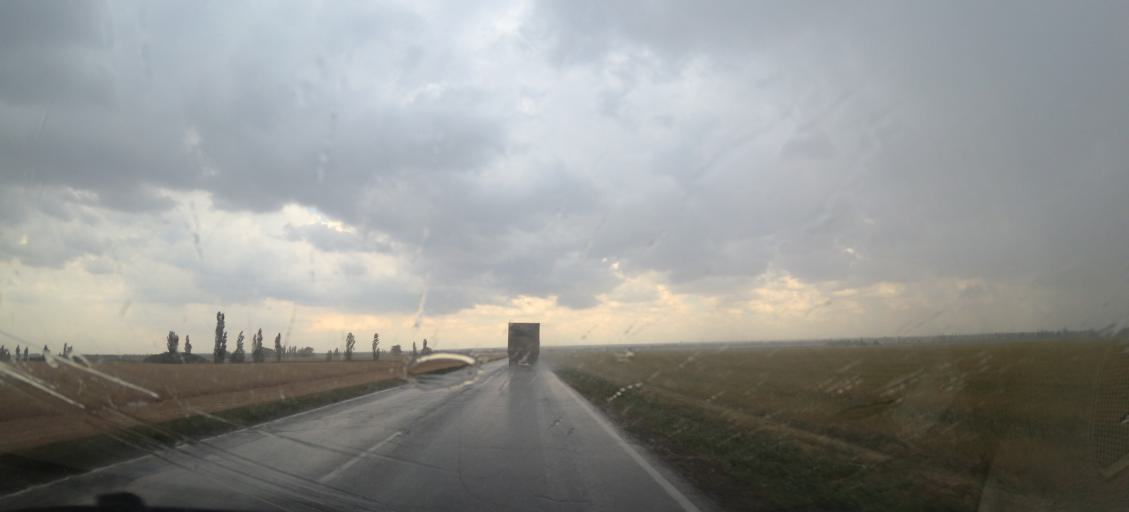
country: RU
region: Rostov
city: Orlovskiy
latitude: 46.8647
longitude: 41.9607
